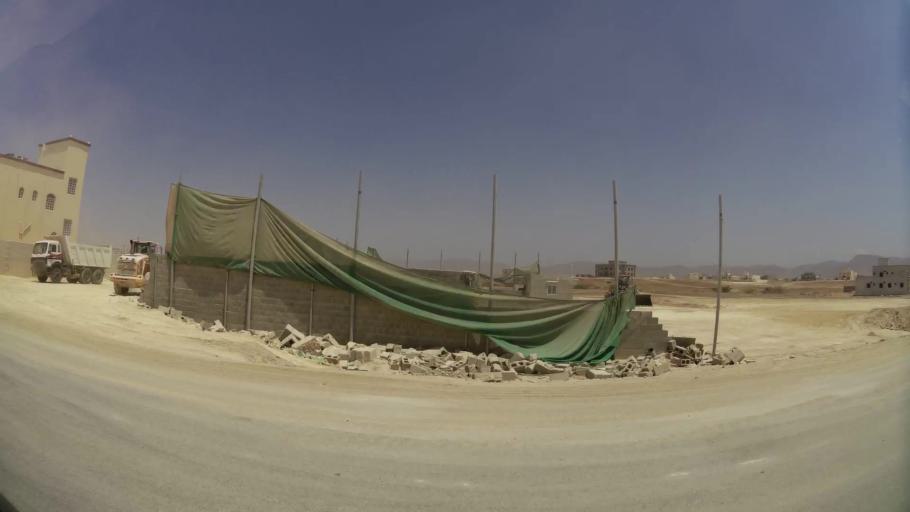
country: OM
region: Zufar
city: Salalah
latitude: 17.0890
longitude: 54.1962
